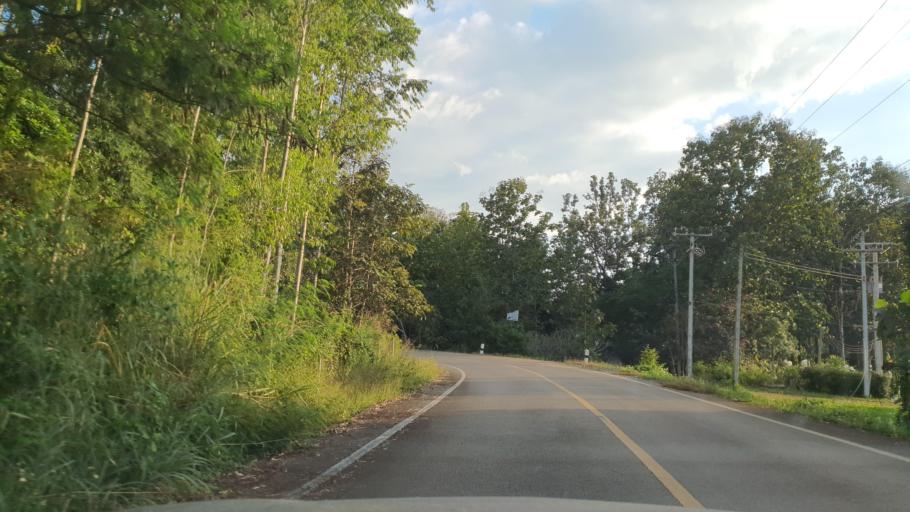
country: TH
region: Chiang Mai
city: Mae On
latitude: 18.8554
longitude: 99.2470
